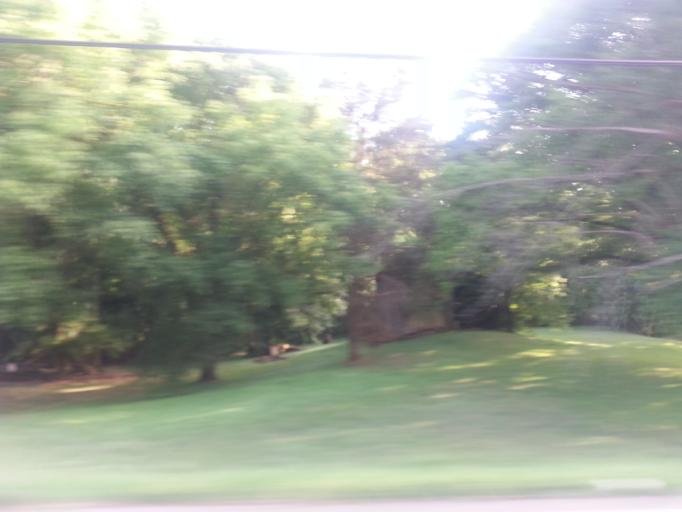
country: US
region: Tennessee
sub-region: Loudon County
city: Greenback
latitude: 35.7579
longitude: -84.1326
